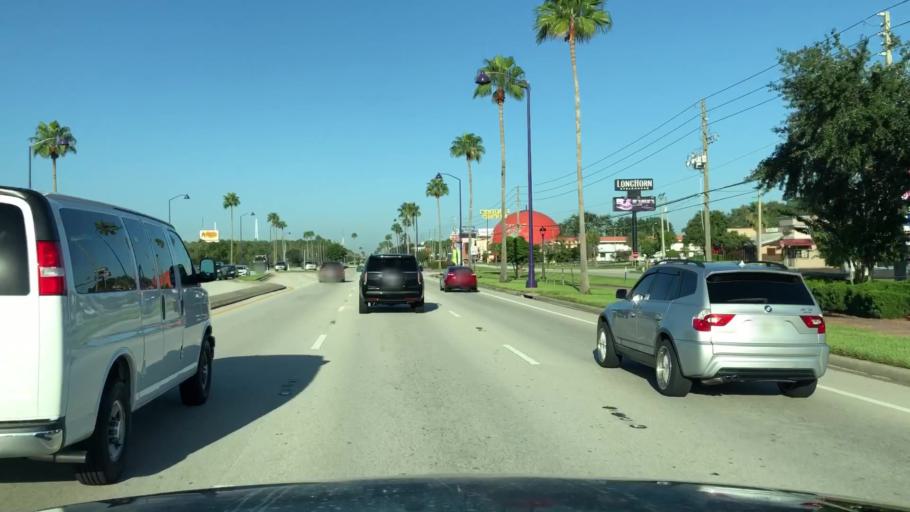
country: US
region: Florida
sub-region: Osceola County
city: Celebration
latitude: 28.3330
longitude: -81.4964
